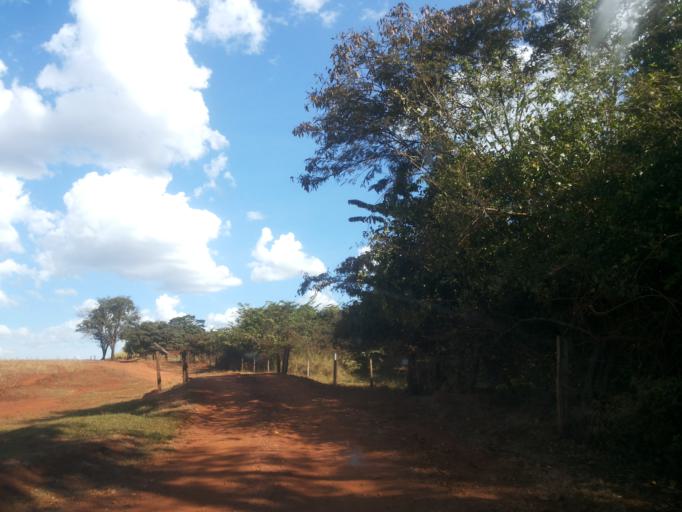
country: BR
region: Minas Gerais
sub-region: Capinopolis
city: Capinopolis
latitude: -18.5845
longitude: -49.4952
